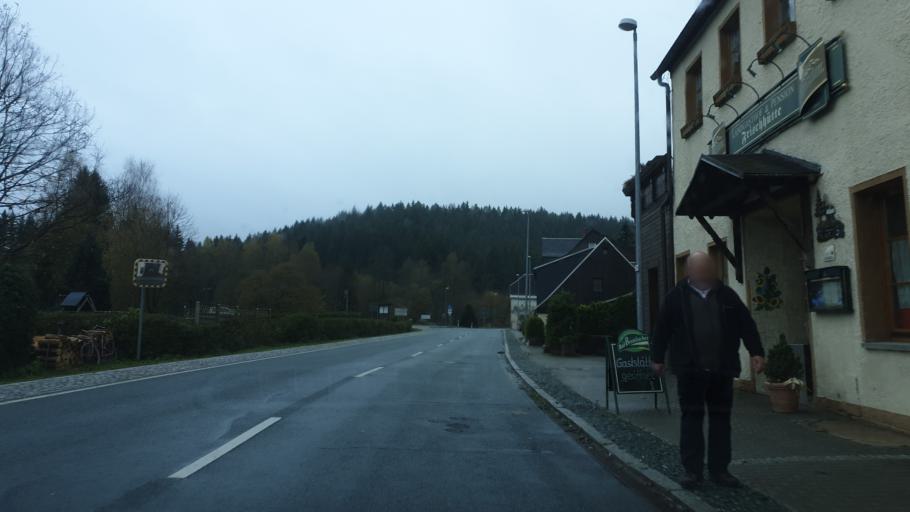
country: DE
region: Saxony
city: Muldenhammer
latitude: 50.4602
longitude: 12.4902
